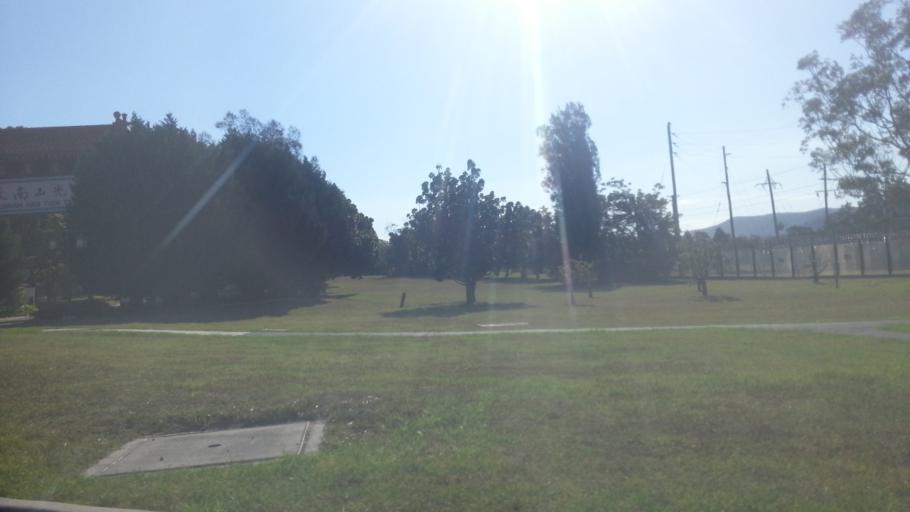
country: AU
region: New South Wales
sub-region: Wollongong
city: Berkeley
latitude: -34.4638
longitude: 150.8541
